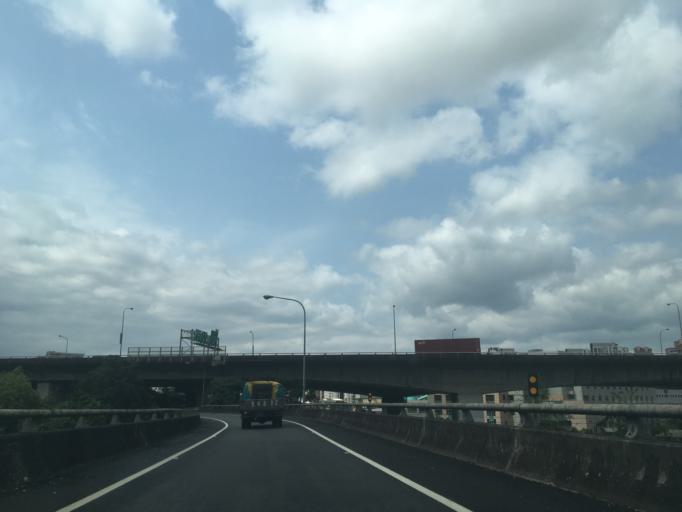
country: TW
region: Taipei
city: Taipei
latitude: 25.0598
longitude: 121.6429
